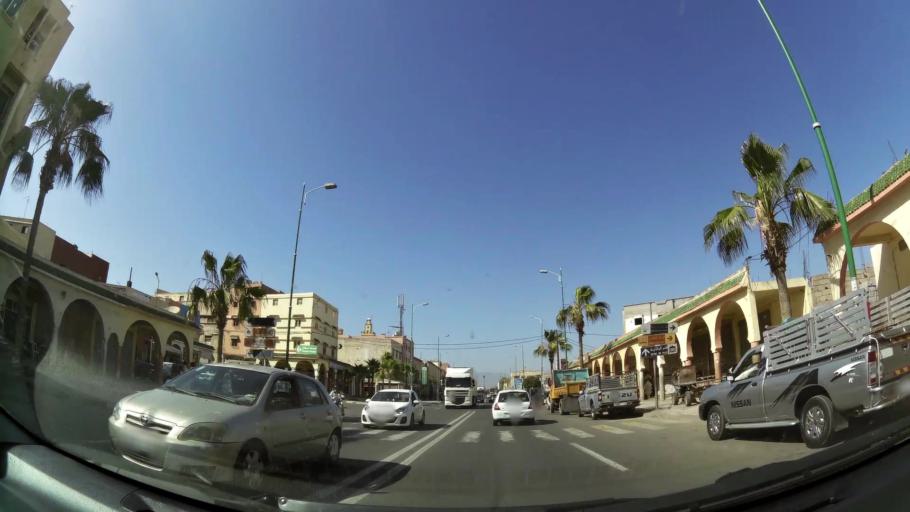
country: MA
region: Souss-Massa-Draa
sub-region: Inezgane-Ait Mellou
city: Inezgane
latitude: 30.3660
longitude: -9.5331
